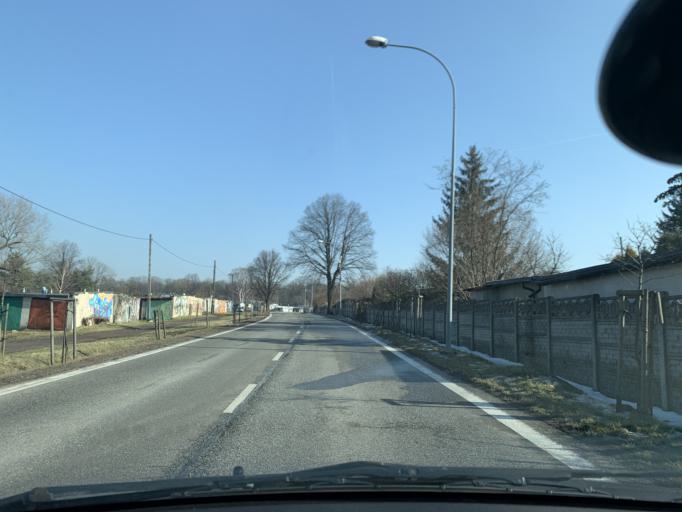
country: PL
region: Silesian Voivodeship
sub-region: Bytom
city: Bytom
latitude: 50.3598
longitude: 18.9174
